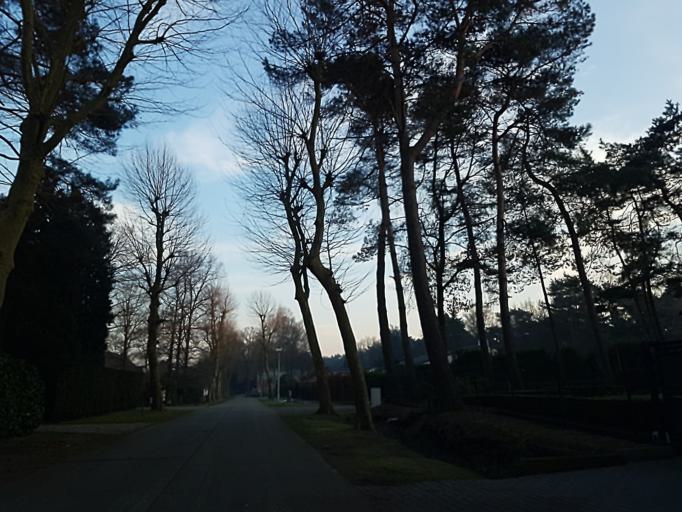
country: BE
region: Flanders
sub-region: Provincie Antwerpen
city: Brecht
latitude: 51.3244
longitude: 4.5941
